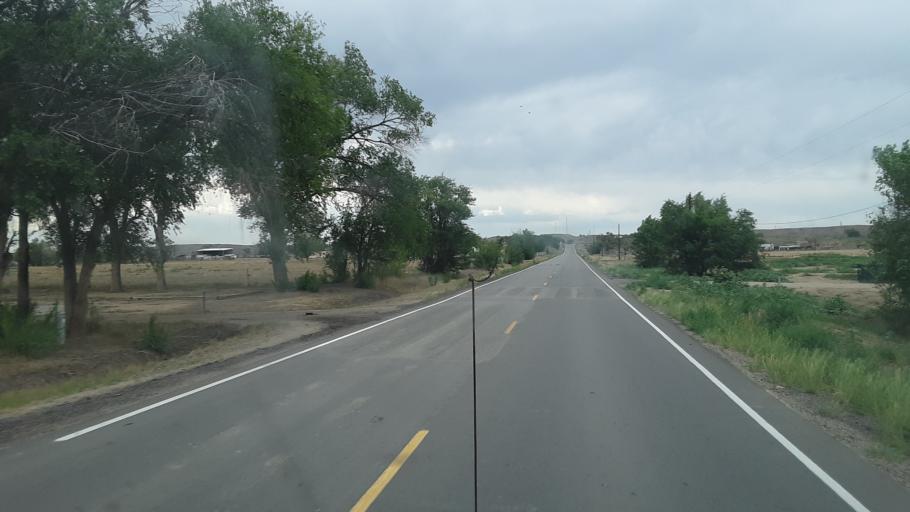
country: US
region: Colorado
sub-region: Otero County
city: Fowler
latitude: 38.1486
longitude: -104.0231
